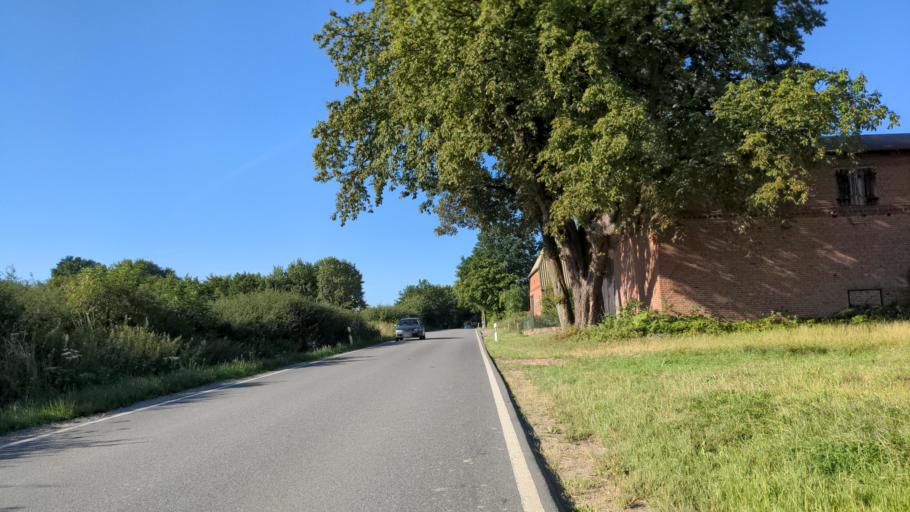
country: DE
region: Mecklenburg-Vorpommern
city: Dassow
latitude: 53.8765
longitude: 10.9515
